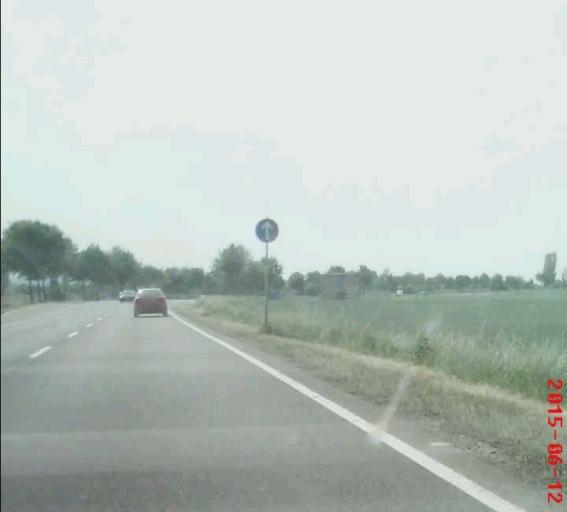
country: DE
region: Saxony-Anhalt
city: Wallhausen
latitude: 51.4597
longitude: 11.2476
